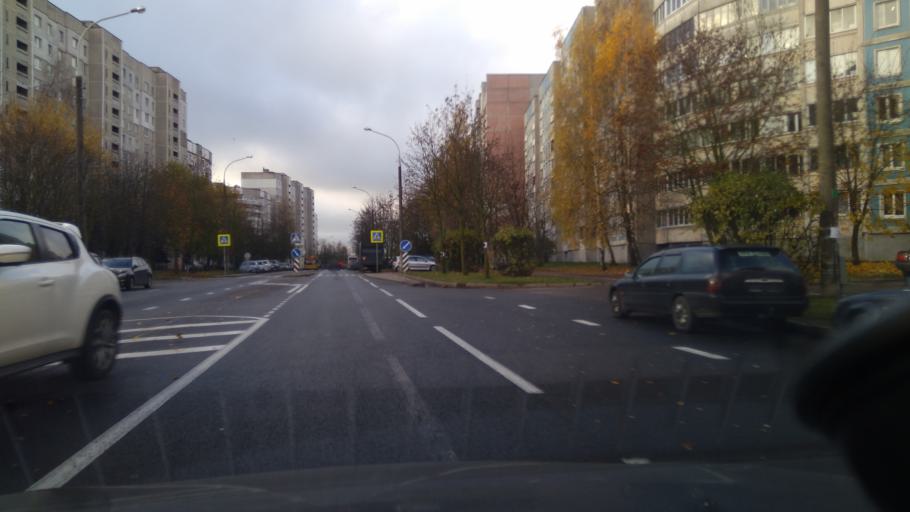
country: BY
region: Minsk
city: Malinovka
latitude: 53.8592
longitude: 27.4365
